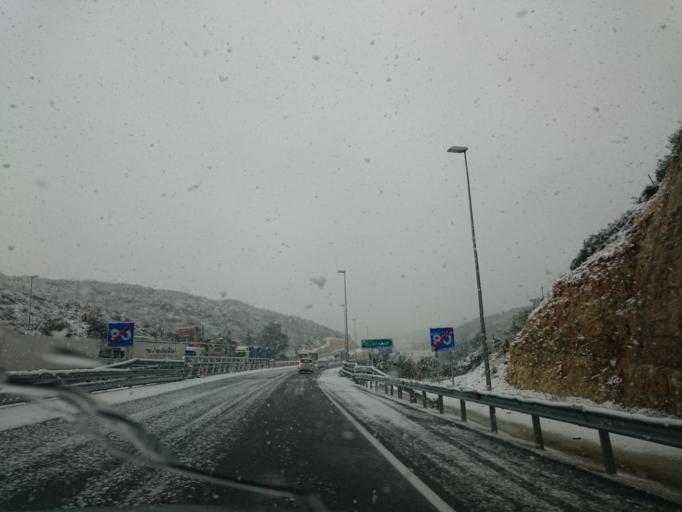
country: ES
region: Catalonia
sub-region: Provincia de Barcelona
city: Sant Pere de Ribes
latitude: 41.2983
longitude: 1.7267
